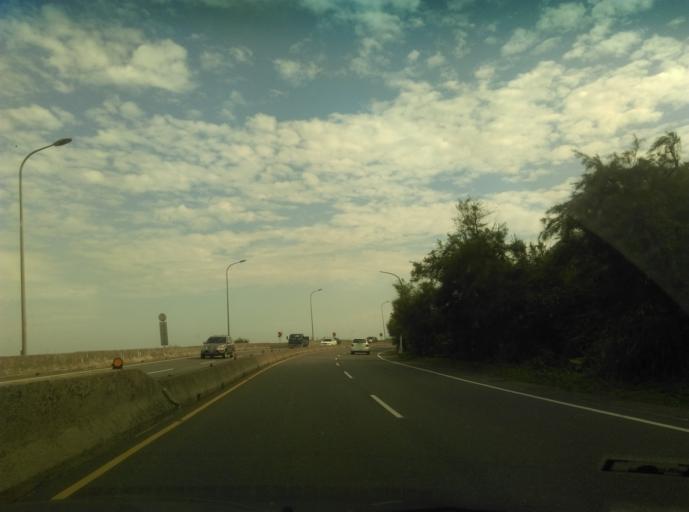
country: TW
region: Taiwan
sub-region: Keelung
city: Keelung
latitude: 25.1791
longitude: 121.7008
